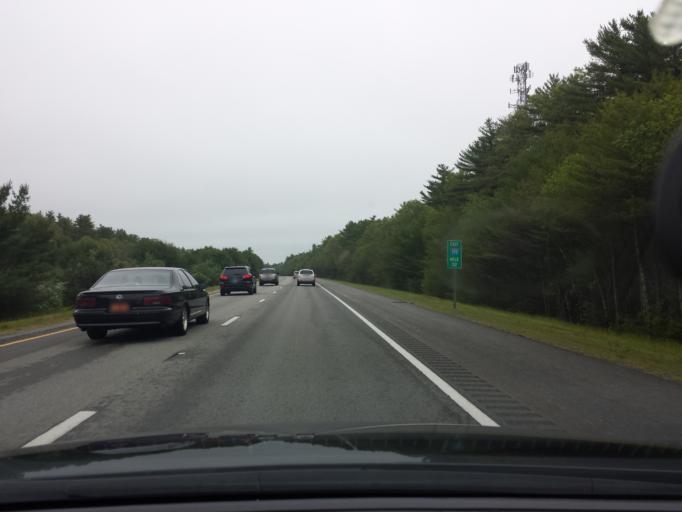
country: US
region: Massachusetts
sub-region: Plymouth County
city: Mattapoisett Center
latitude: 41.6864
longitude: -70.8086
